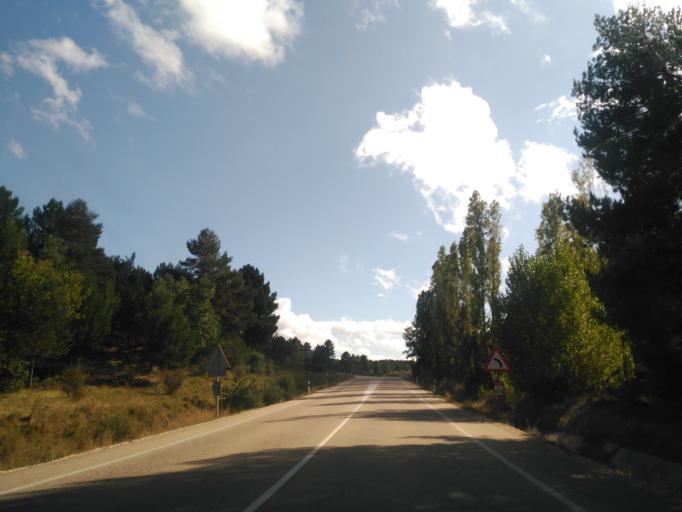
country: ES
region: Castille and Leon
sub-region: Provincia de Burgos
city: Pinilla de los Barruecos
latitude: 41.9091
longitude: -3.2759
